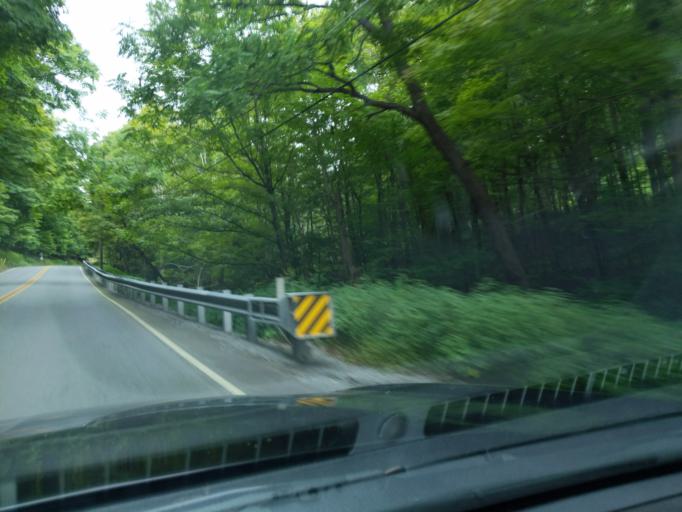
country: US
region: Pennsylvania
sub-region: Blair County
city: Claysburg
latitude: 40.3559
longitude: -78.4922
